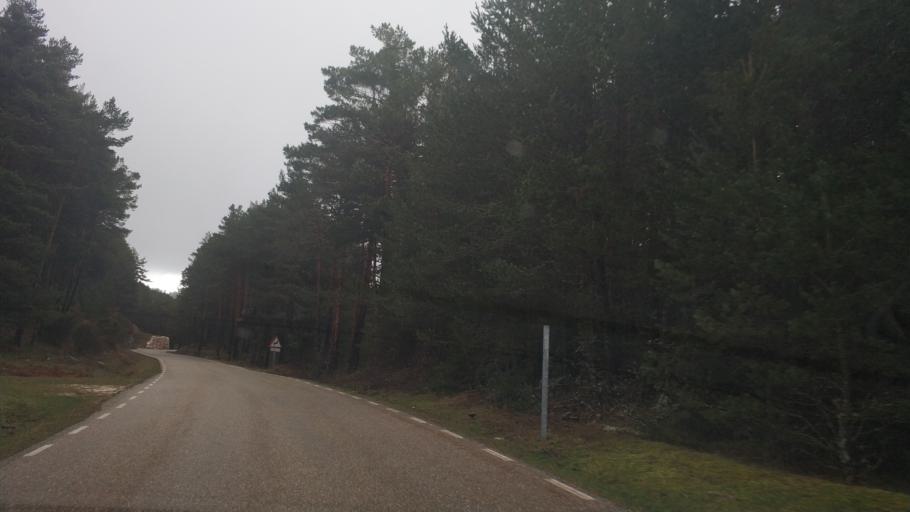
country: ES
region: Castille and Leon
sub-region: Provincia de Burgos
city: Neila
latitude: 42.0216
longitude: -3.0146
